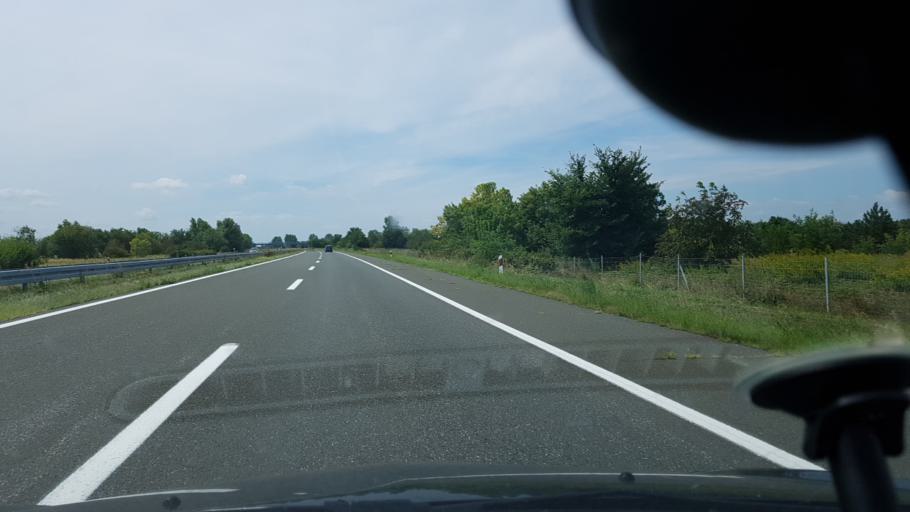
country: HR
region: Medimurska
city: Domasinec
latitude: 46.4119
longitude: 16.6043
